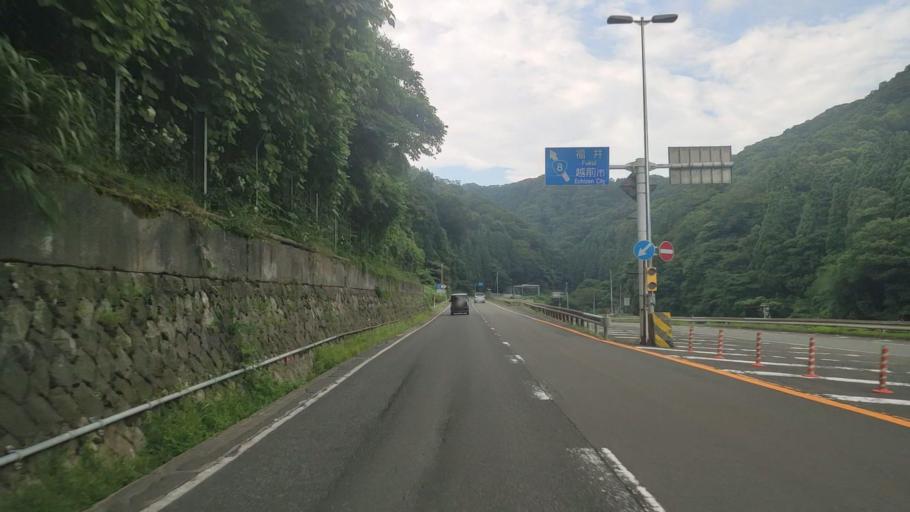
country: JP
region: Fukui
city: Takefu
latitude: 35.8361
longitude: 136.1207
